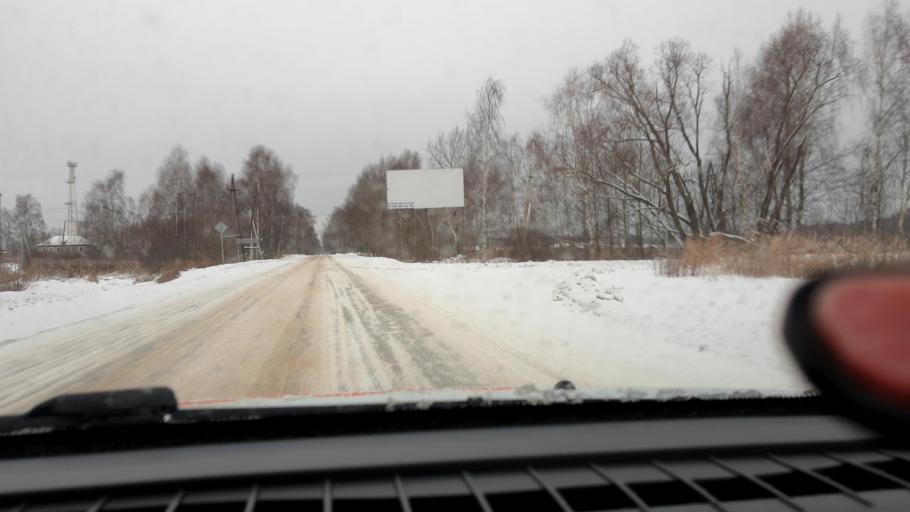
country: RU
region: Nizjnij Novgorod
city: Pamyat' Parizhskoy Kommuny
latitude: 56.2659
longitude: 44.4355
